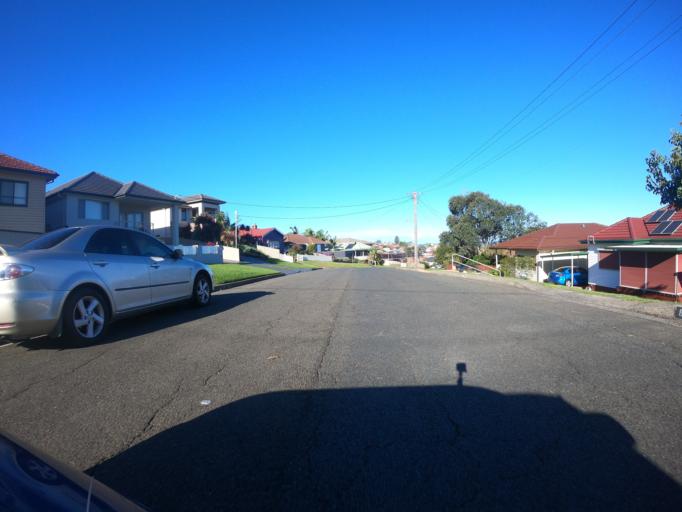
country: AU
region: New South Wales
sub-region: Wollongong
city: Port Kembla
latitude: -34.4862
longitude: 150.8988
